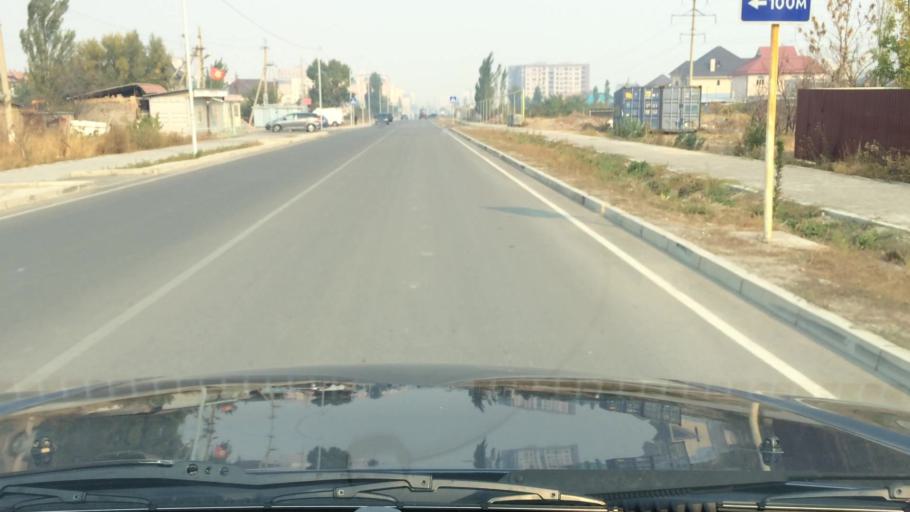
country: KG
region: Chuy
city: Bishkek
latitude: 42.8243
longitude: 74.5698
